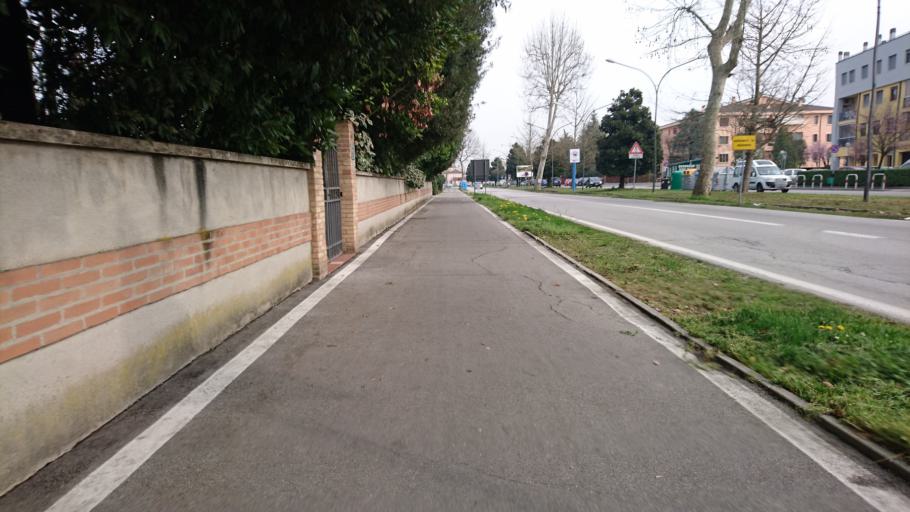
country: IT
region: Veneto
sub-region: Provincia di Padova
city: Abano Terme
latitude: 45.3619
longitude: 11.7974
